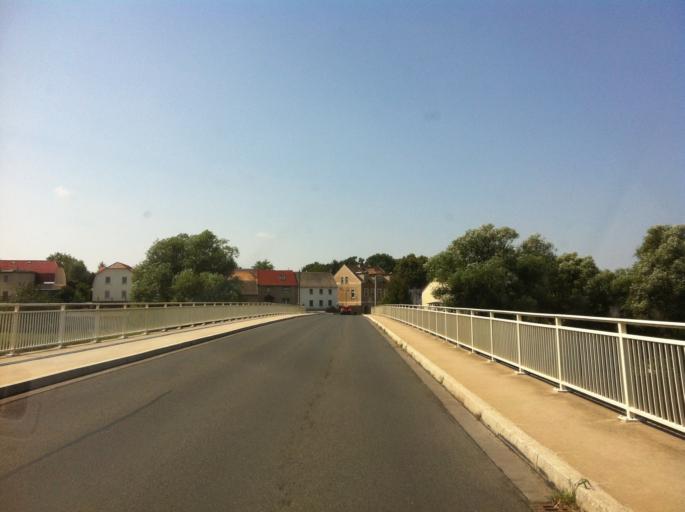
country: DE
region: Saxony
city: Trebsen
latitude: 51.2883
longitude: 12.7613
